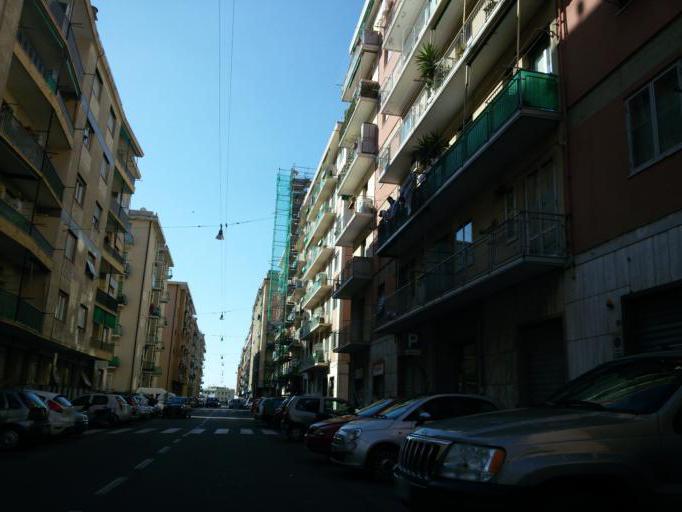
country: IT
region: Liguria
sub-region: Provincia di Genova
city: Genoa
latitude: 44.4238
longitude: 8.9163
